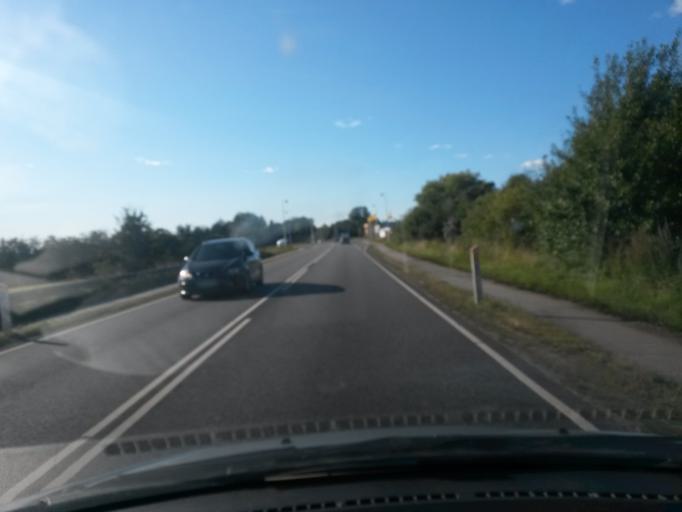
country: DK
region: Central Jutland
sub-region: Arhus Kommune
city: Sabro
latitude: 56.2069
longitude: 10.0394
